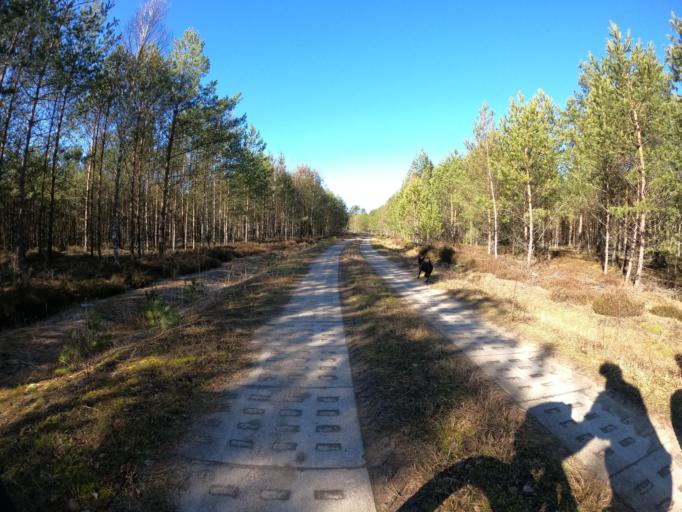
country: PL
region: Greater Poland Voivodeship
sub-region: Powiat zlotowski
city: Sypniewo
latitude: 53.5132
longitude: 16.6452
